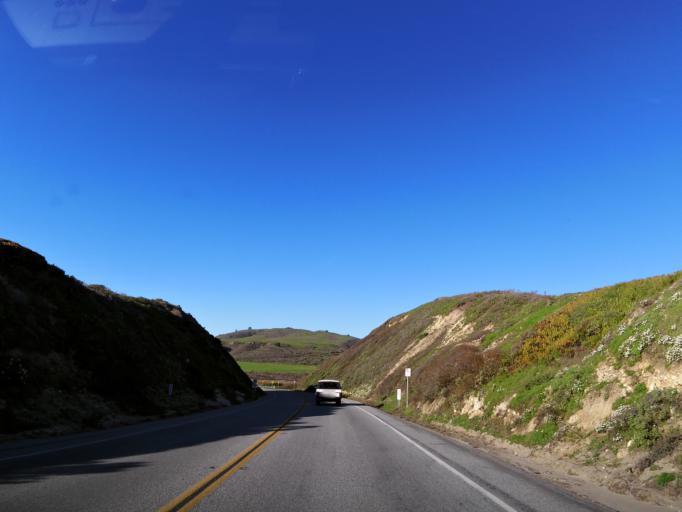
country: US
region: California
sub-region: Santa Cruz County
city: Bonny Doon
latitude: 37.0373
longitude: -122.2267
